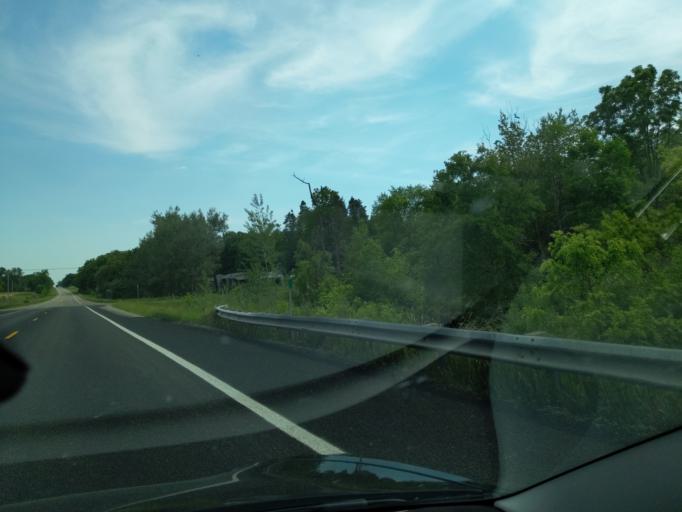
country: US
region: Michigan
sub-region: Barry County
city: Nashville
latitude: 42.6845
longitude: -85.0953
